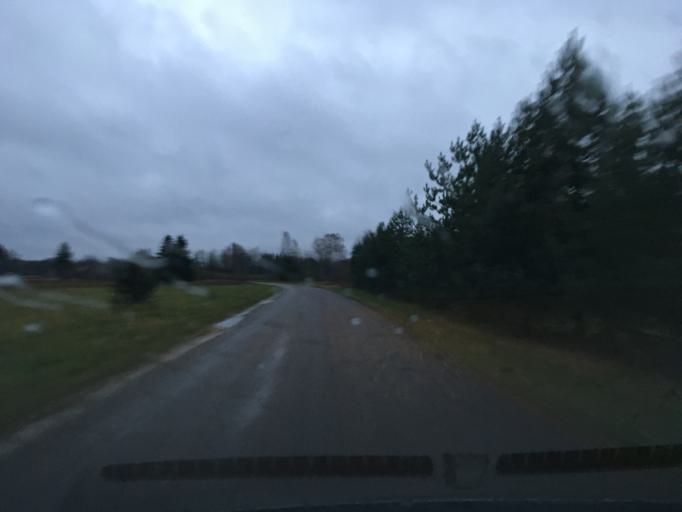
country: EE
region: Laeaene
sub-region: Lihula vald
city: Lihula
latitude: 58.5757
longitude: 23.7396
